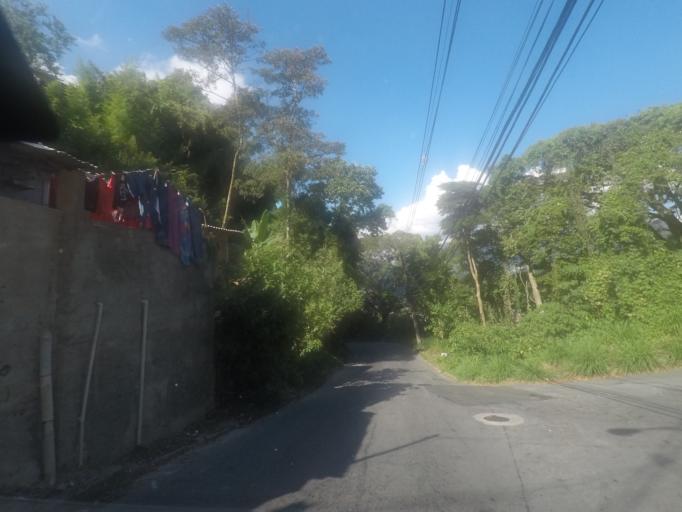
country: BR
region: Rio de Janeiro
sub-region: Petropolis
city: Petropolis
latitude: -22.5222
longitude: -43.1979
